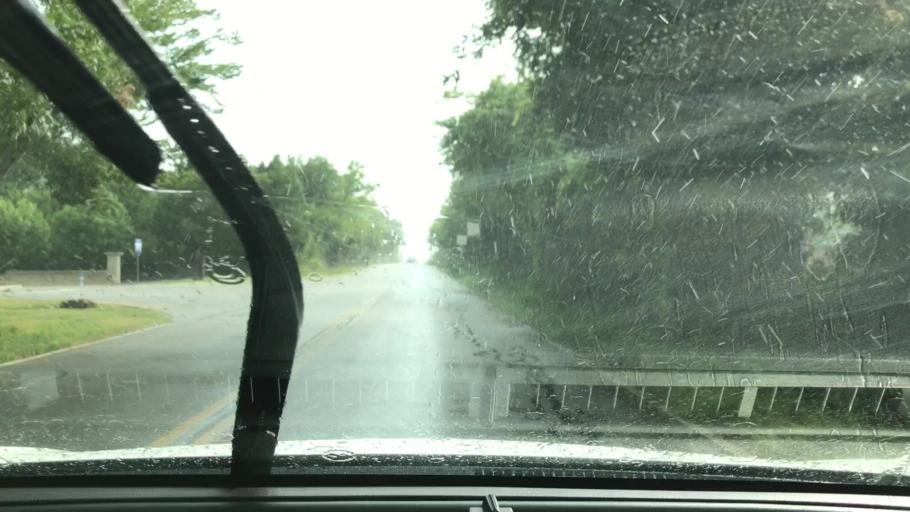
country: US
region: Texas
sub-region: Rockwall County
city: Rockwall
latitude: 32.9510
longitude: -96.5204
